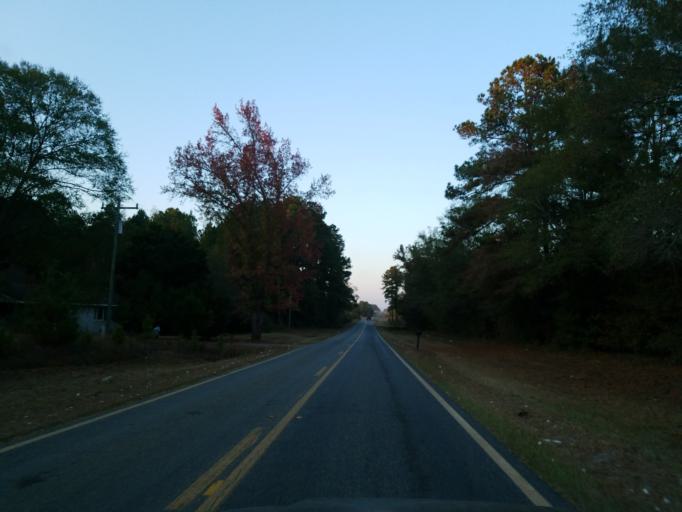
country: US
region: Georgia
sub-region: Ben Hill County
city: Fitzgerald
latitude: 31.6936
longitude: -83.3852
